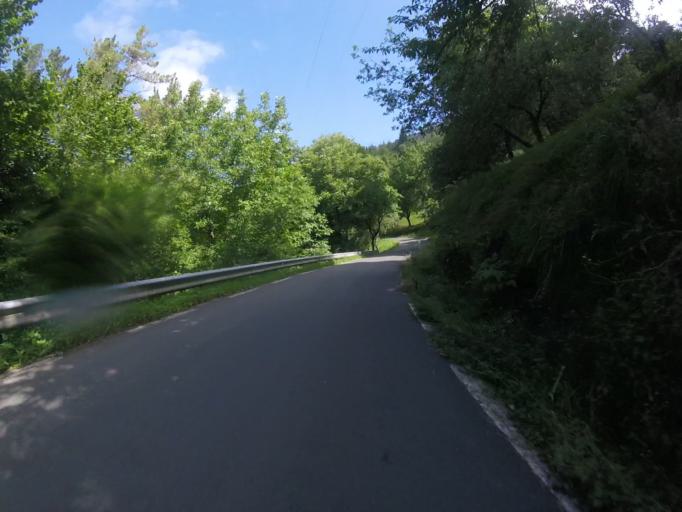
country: ES
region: Basque Country
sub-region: Provincia de Guipuzcoa
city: Beasain
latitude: 43.0813
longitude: -2.2275
